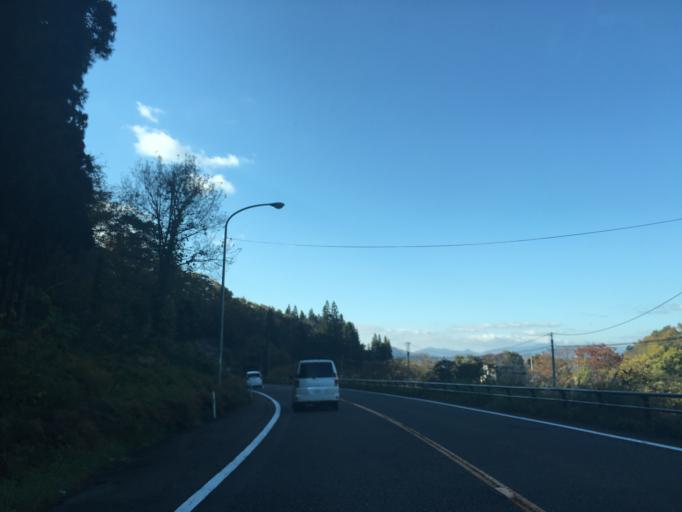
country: JP
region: Fukushima
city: Kitakata
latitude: 37.5706
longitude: 139.6682
